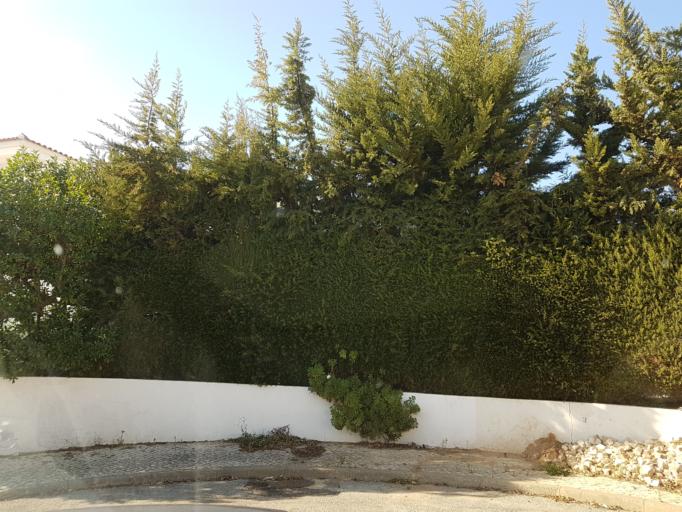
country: PT
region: Faro
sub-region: Albufeira
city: Ferreiras
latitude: 37.0950
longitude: -8.1983
